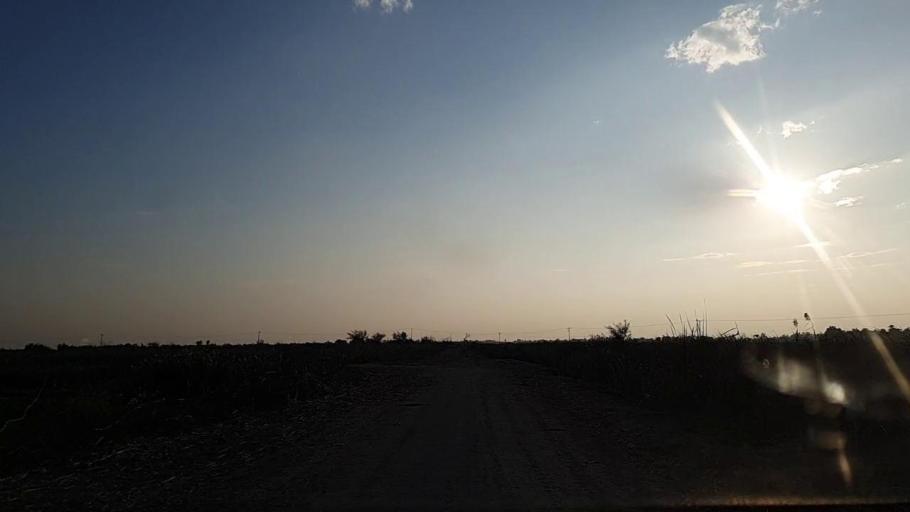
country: PK
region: Sindh
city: Sanghar
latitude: 26.2605
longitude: 68.9778
